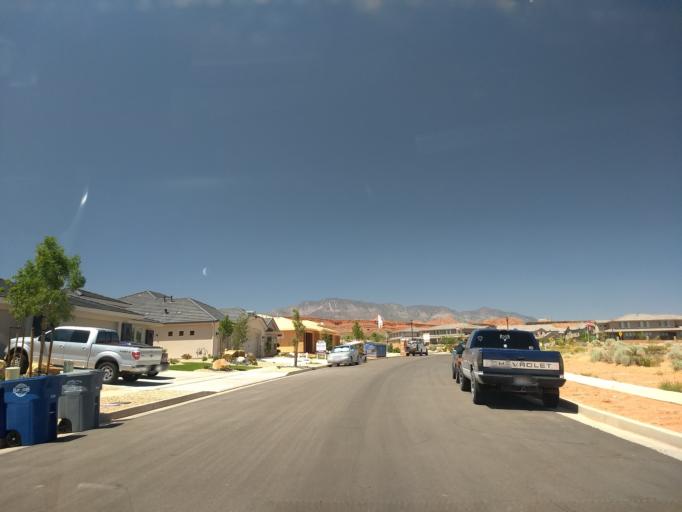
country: US
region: Utah
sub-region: Washington County
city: Washington
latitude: 37.1430
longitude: -113.4793
